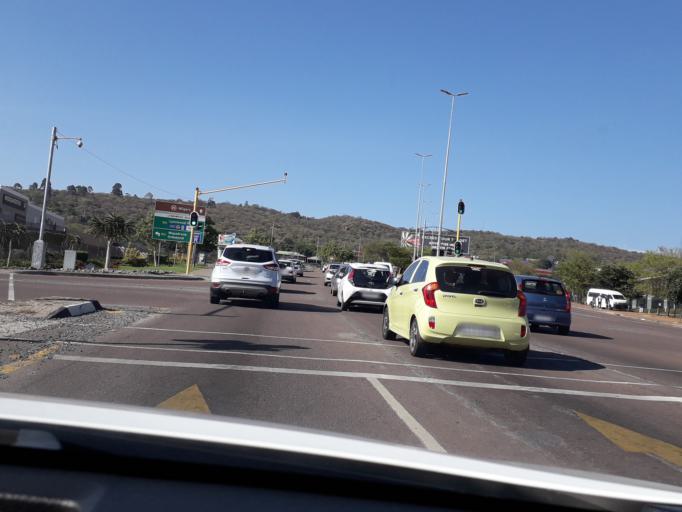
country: ZA
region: Gauteng
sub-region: City of Tshwane Metropolitan Municipality
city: Pretoria
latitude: -25.7643
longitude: 28.3227
